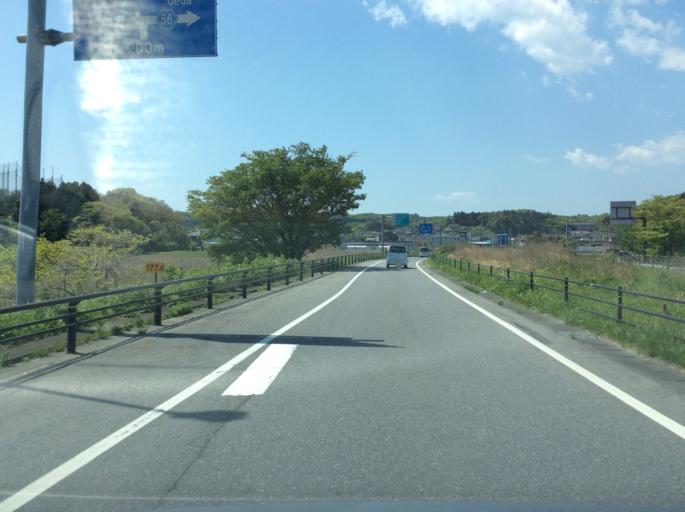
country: JP
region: Ibaraki
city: Kitaibaraki
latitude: 36.8904
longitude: 140.7861
